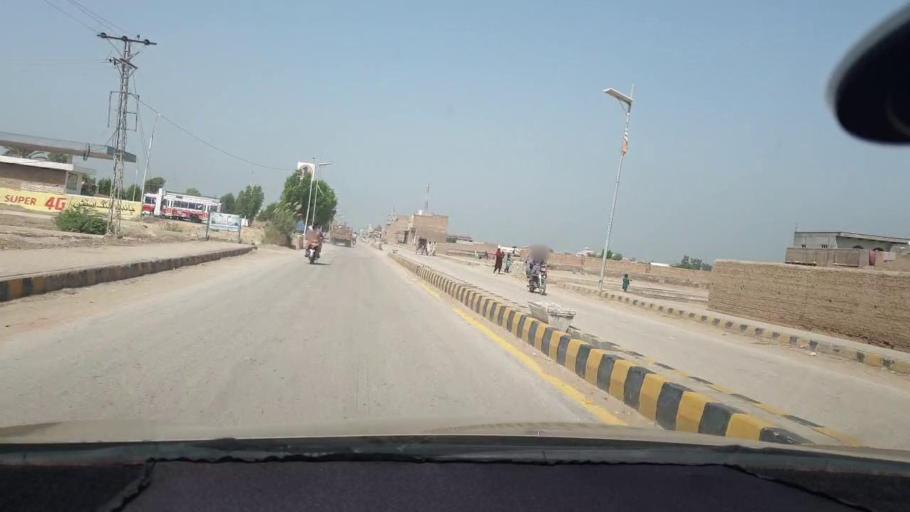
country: PK
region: Sindh
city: Kambar
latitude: 27.5888
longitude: 68.0172
